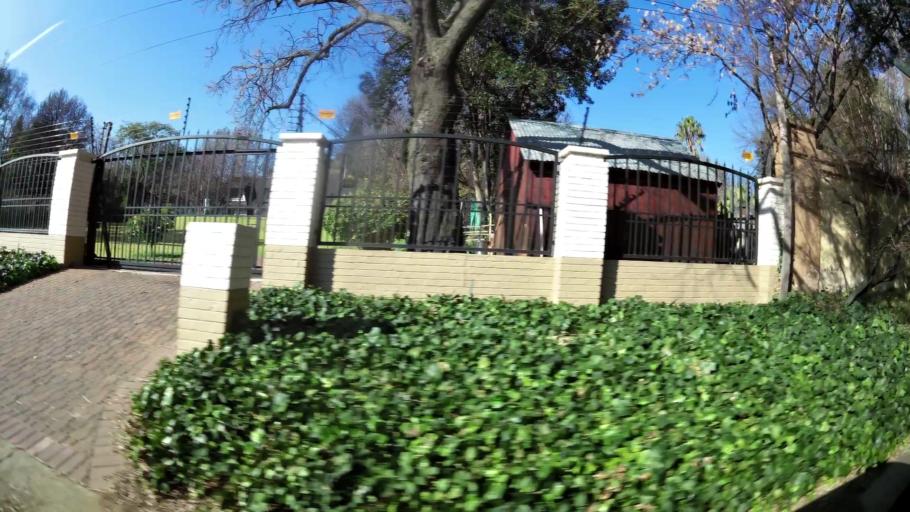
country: ZA
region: Gauteng
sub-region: City of Johannesburg Metropolitan Municipality
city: Midrand
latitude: -26.0630
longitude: 28.0442
